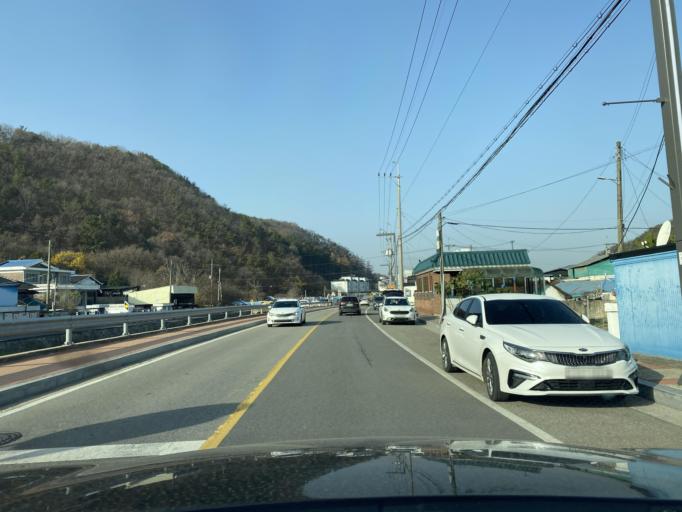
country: KR
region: Chungcheongnam-do
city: Yesan
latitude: 36.6763
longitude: 126.8446
